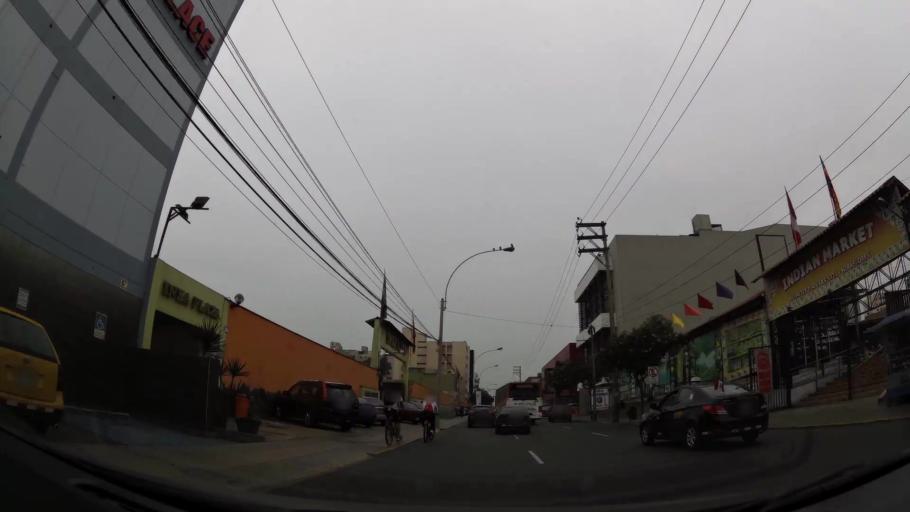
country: PE
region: Lima
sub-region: Lima
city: San Isidro
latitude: -12.1163
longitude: -77.0283
